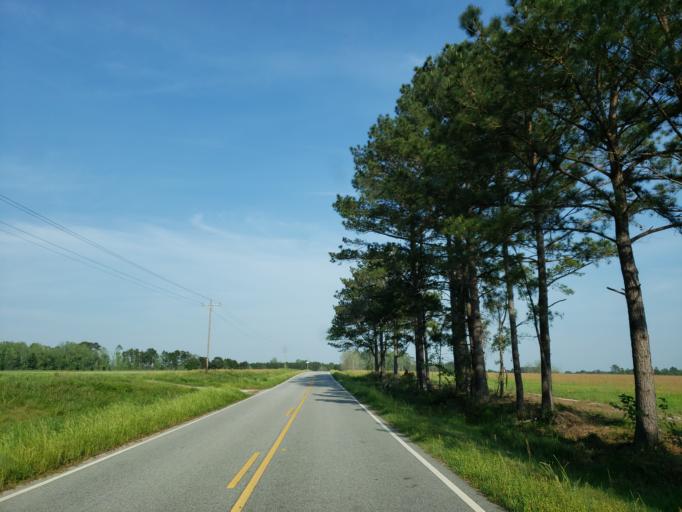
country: US
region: Georgia
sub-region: Tift County
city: Tifton
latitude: 31.5760
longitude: -83.4927
